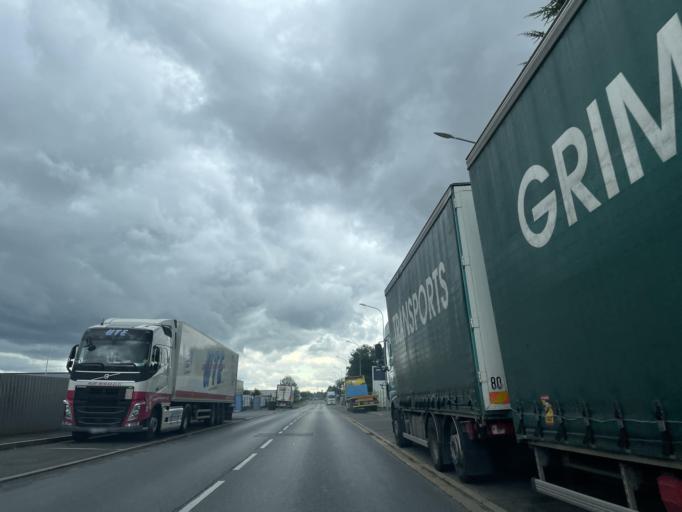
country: FR
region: Ile-de-France
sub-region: Departement de Seine-et-Marne
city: Fublaines
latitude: 48.9598
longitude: 2.9158
